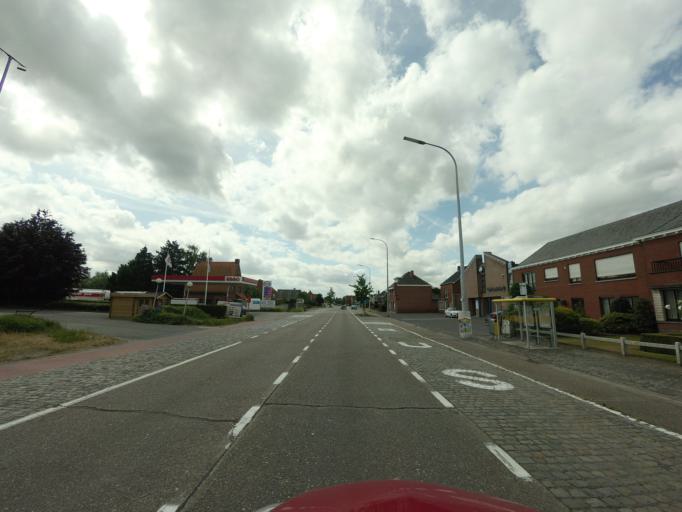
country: BE
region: Flanders
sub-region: Provincie Oost-Vlaanderen
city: Maldegem
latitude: 51.2029
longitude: 3.4509
